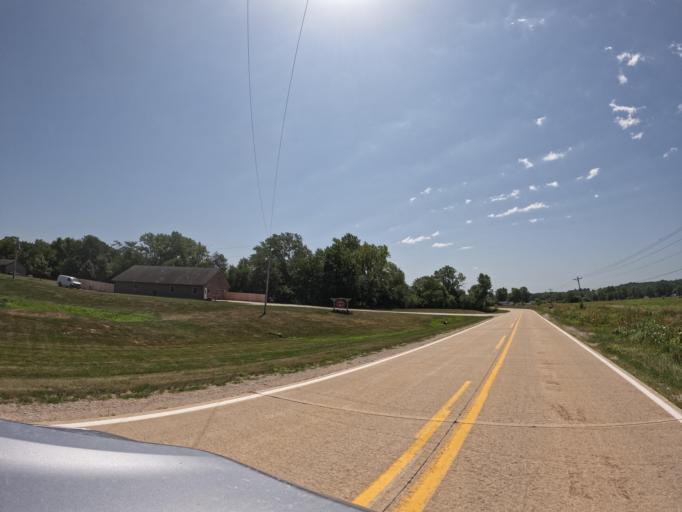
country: US
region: Iowa
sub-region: Henry County
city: Mount Pleasant
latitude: 40.9044
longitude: -91.5543
